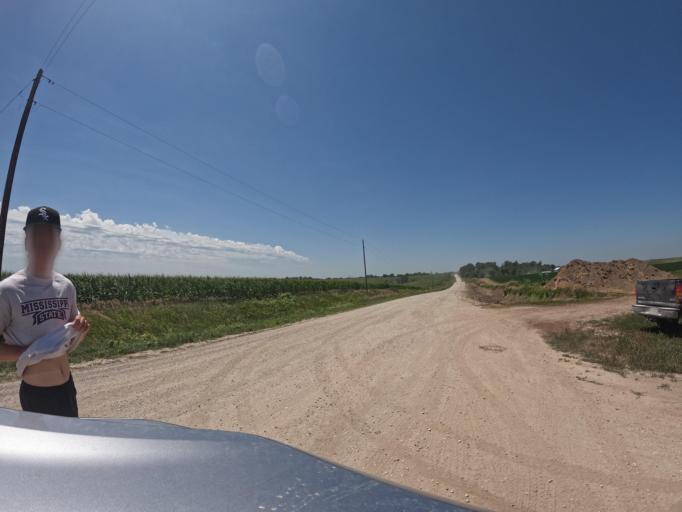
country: US
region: Iowa
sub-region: Keokuk County
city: Sigourney
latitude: 41.4091
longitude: -92.3121
